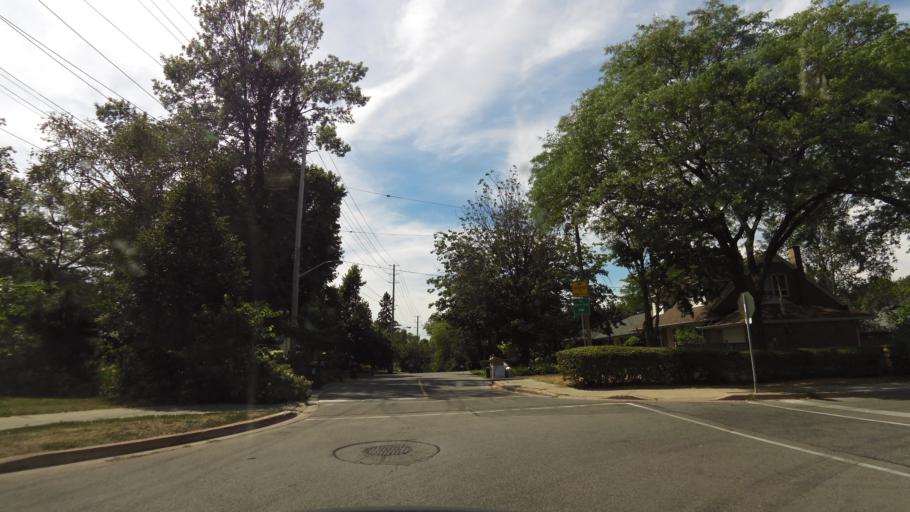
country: CA
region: Ontario
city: Etobicoke
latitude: 43.6349
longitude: -79.4995
